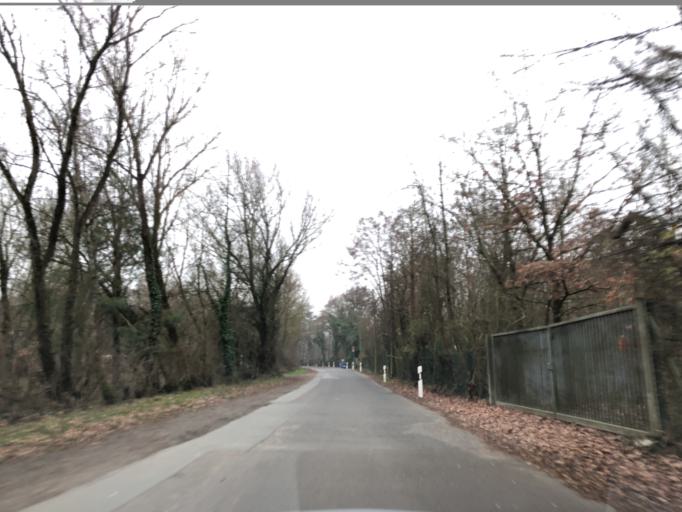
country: DE
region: Hesse
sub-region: Regierungsbezirk Darmstadt
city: Hanau am Main
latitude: 50.0908
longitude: 8.9053
